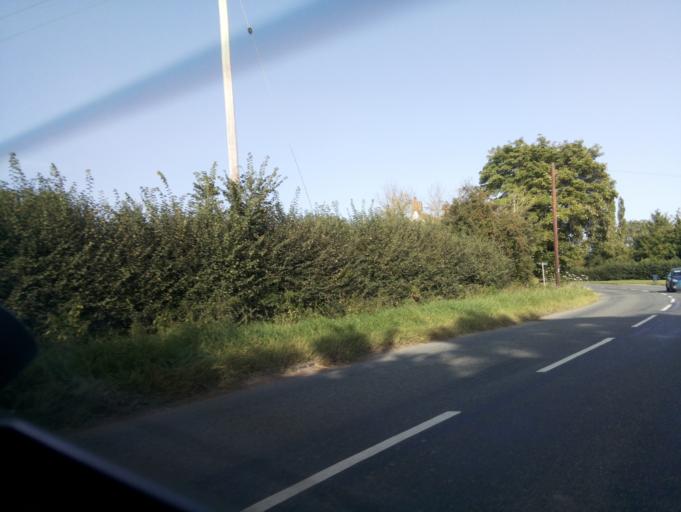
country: GB
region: England
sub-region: Gloucestershire
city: Tewkesbury
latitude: 51.9442
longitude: -2.2030
